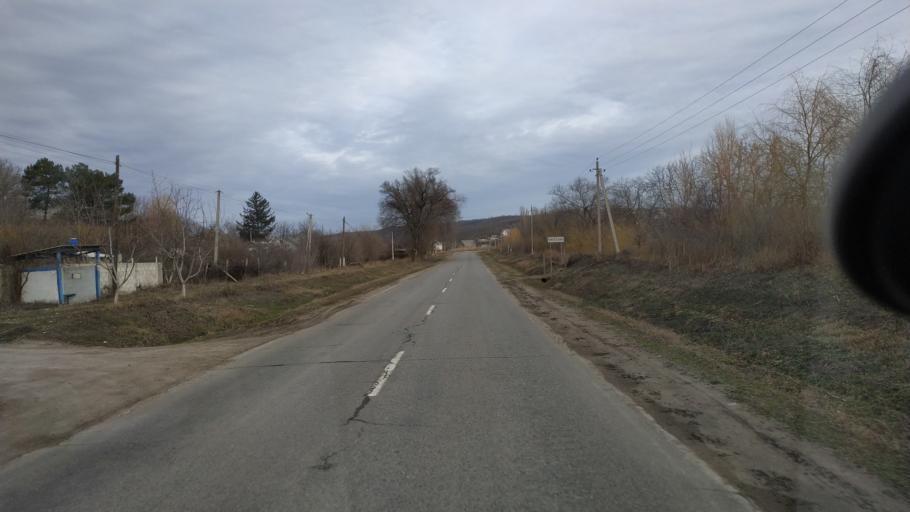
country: MD
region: Chisinau
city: Vadul lui Voda
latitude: 47.1348
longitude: 29.0615
